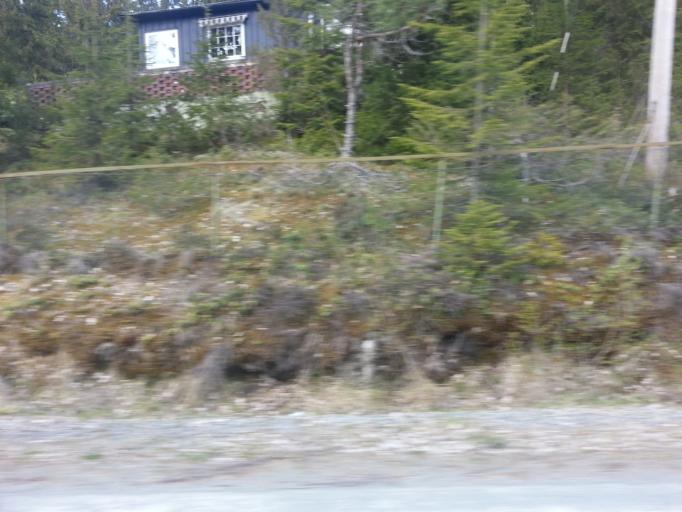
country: NO
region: Nord-Trondelag
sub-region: Levanger
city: Skogn
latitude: 63.6287
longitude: 11.1931
